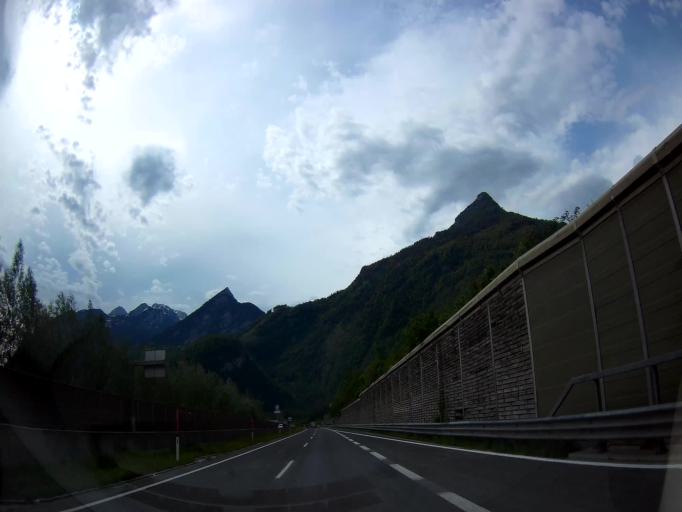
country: AT
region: Salzburg
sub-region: Politischer Bezirk Hallein
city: Golling an der Salzach
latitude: 47.5892
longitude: 13.1527
